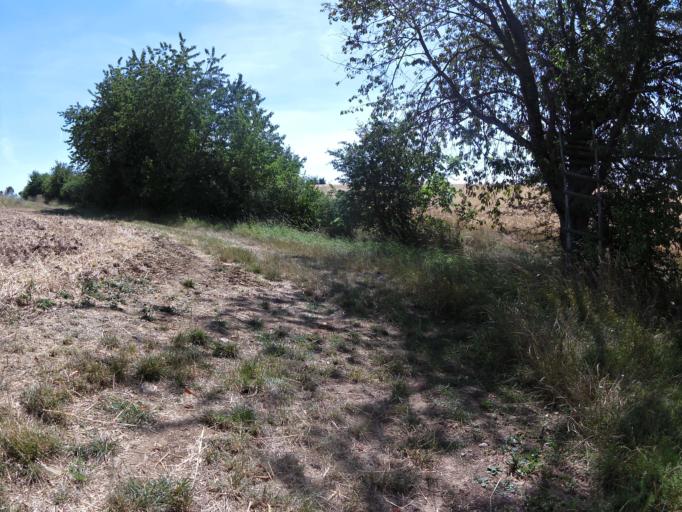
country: DE
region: Bavaria
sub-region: Regierungsbezirk Unterfranken
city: Hettstadt
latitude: 49.8121
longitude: 9.8200
